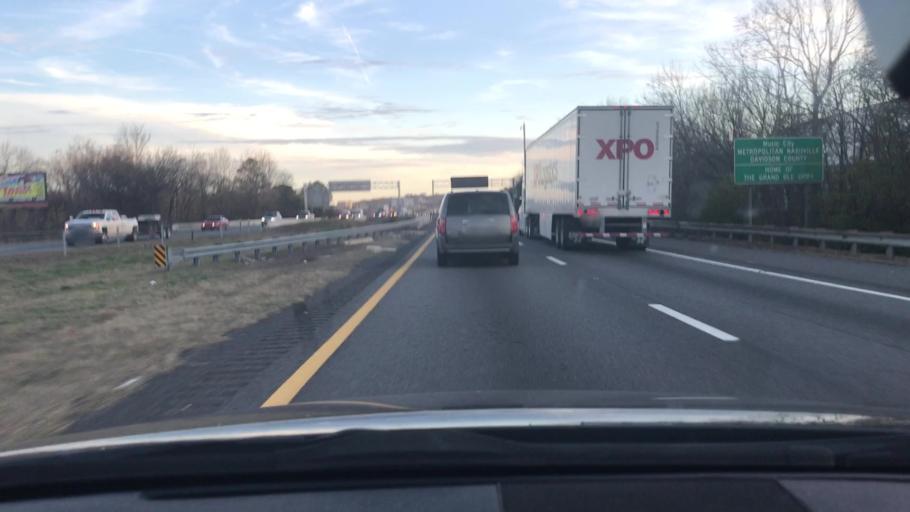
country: US
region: Tennessee
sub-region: Davidson County
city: Goodlettsville
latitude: 36.3347
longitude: -86.7106
